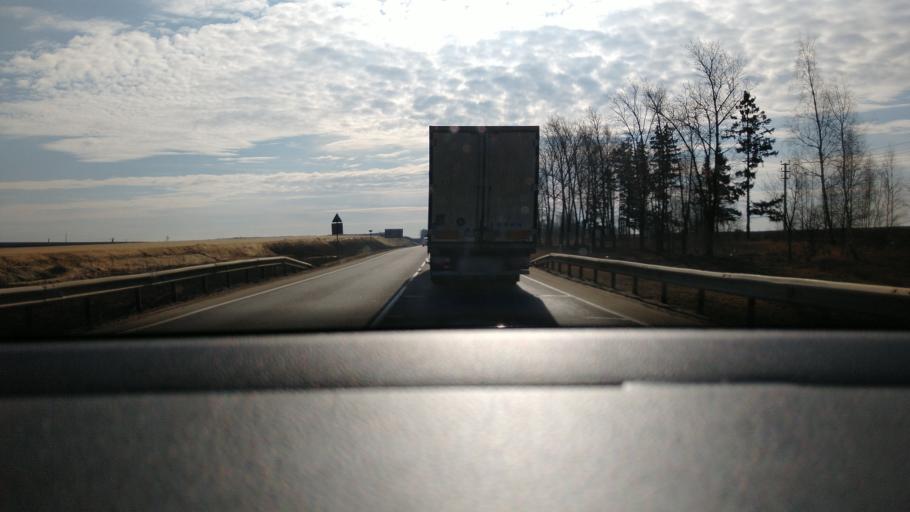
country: RU
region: Moskovskaya
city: Dubrovitsy
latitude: 55.3635
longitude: 37.4295
